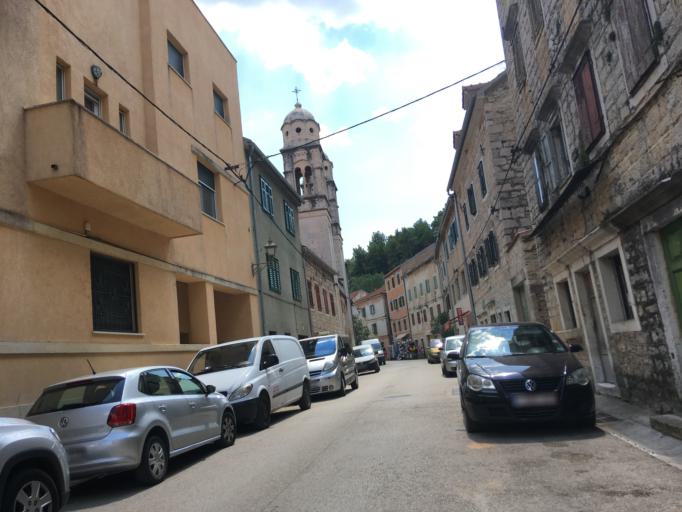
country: HR
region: Sibensko-Kniniska
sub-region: Grad Sibenik
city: Sibenik
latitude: 43.8205
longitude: 15.9223
